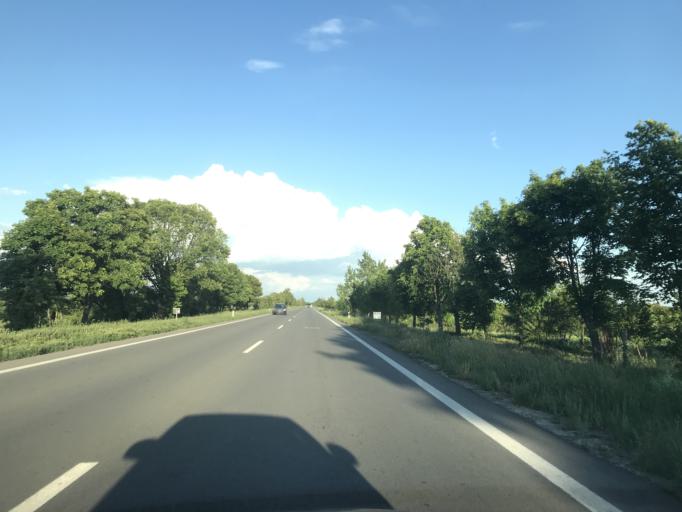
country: RS
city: Aradac
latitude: 45.3874
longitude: 20.3147
